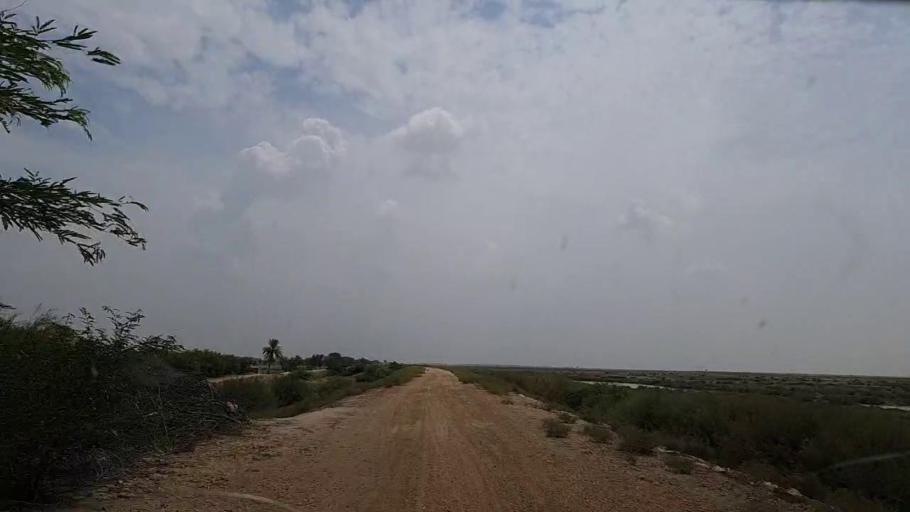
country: PK
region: Sindh
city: Phulji
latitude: 26.8037
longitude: 67.6037
